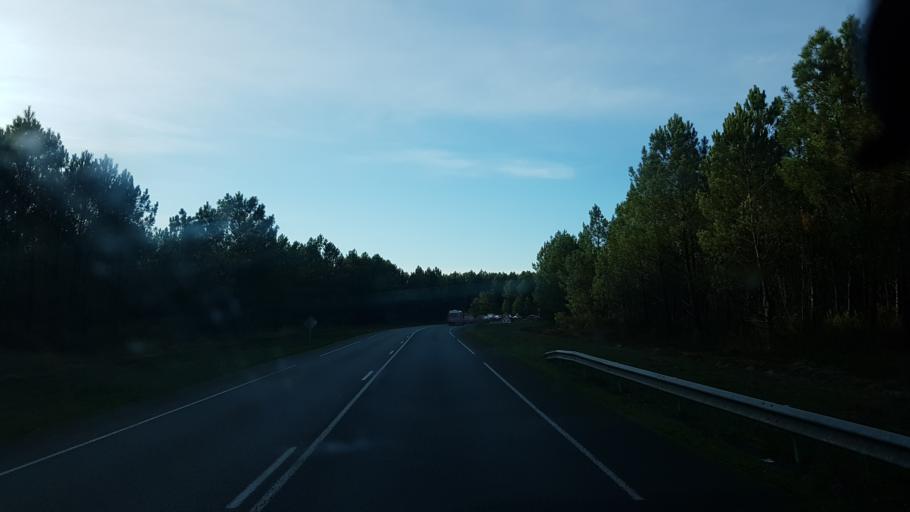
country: FR
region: Aquitaine
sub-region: Departement de la Gironde
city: Martignas-sur-Jalle
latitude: 44.8342
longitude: -0.8010
